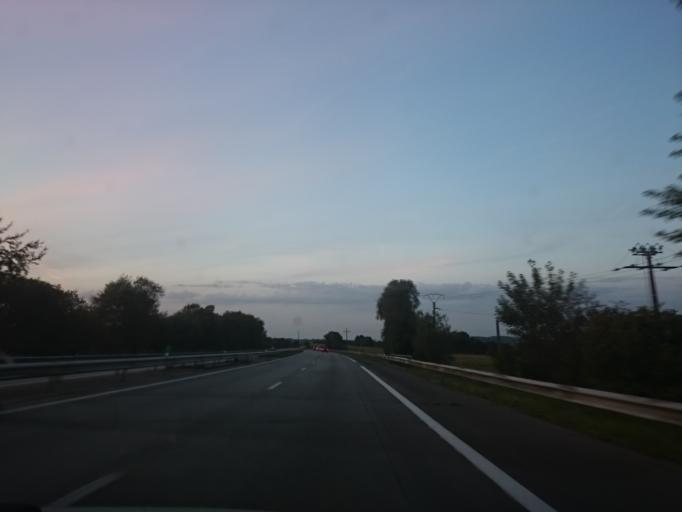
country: FR
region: Brittany
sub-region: Departement du Finistere
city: Briec
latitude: 48.1217
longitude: -4.0224
